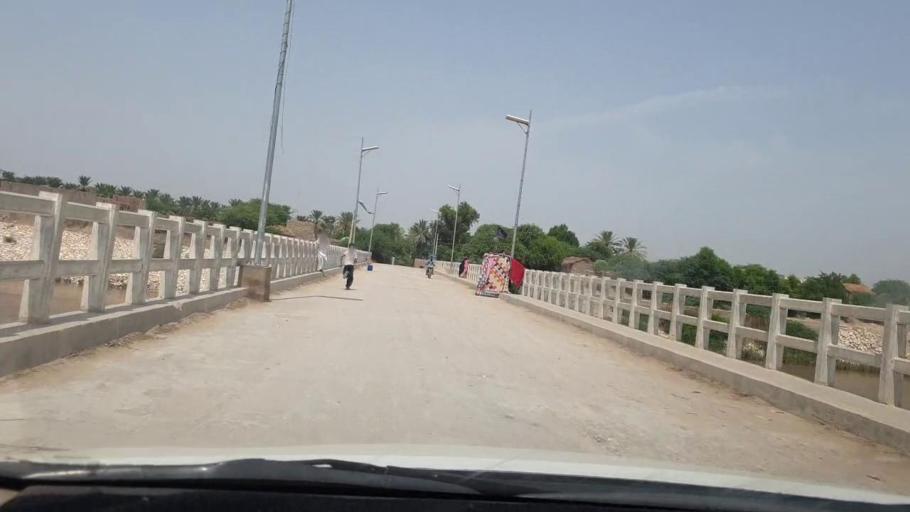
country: PK
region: Sindh
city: Rohri
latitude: 27.4960
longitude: 69.0252
